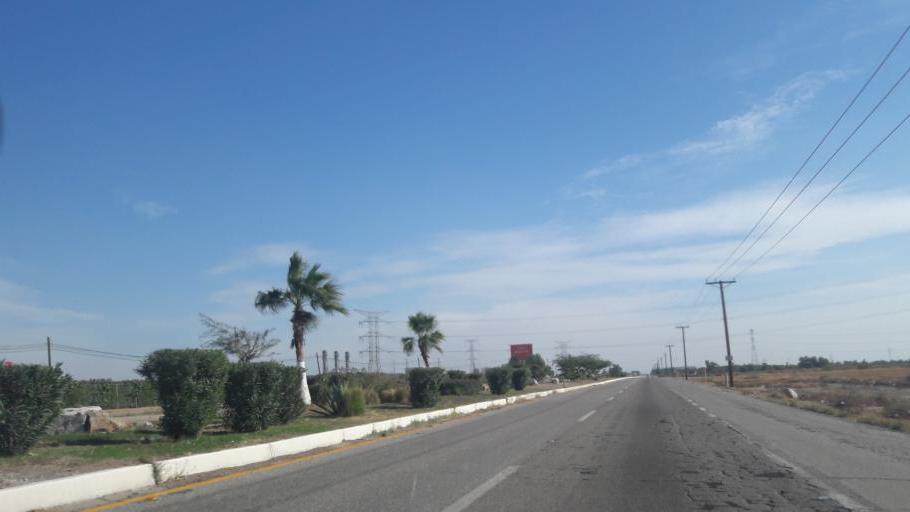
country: MX
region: Baja California
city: Progreso
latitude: 32.5978
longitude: -115.6416
